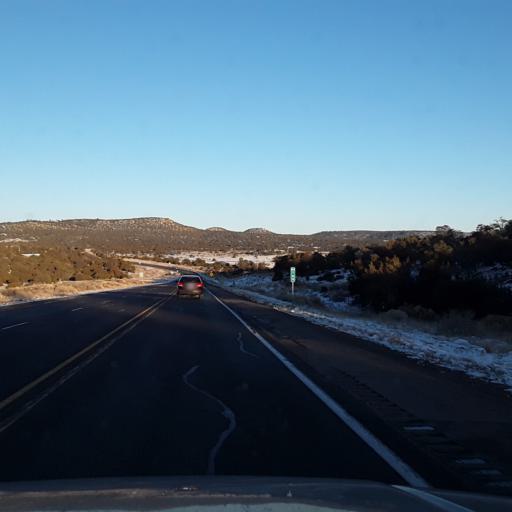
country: US
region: New Mexico
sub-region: Lincoln County
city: Carrizozo
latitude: 34.2386
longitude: -105.6047
